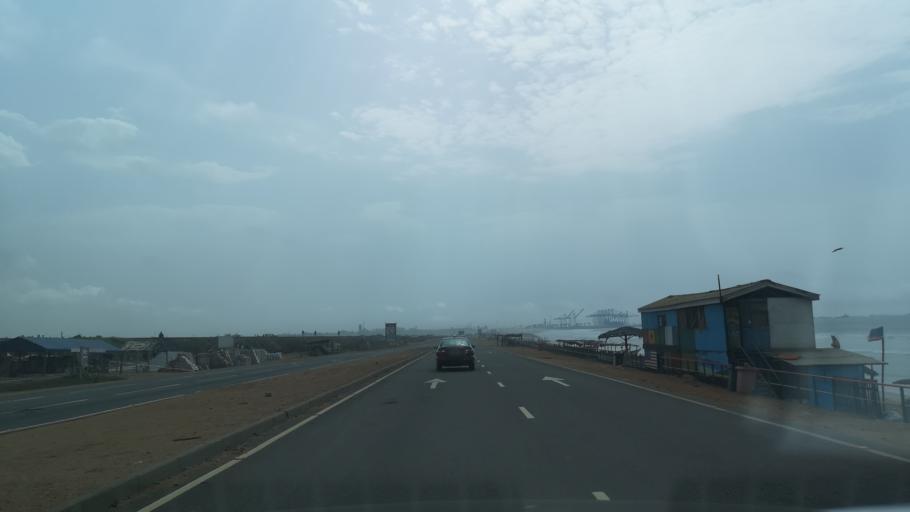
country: GH
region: Greater Accra
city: Nungua
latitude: 5.6114
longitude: -0.0457
